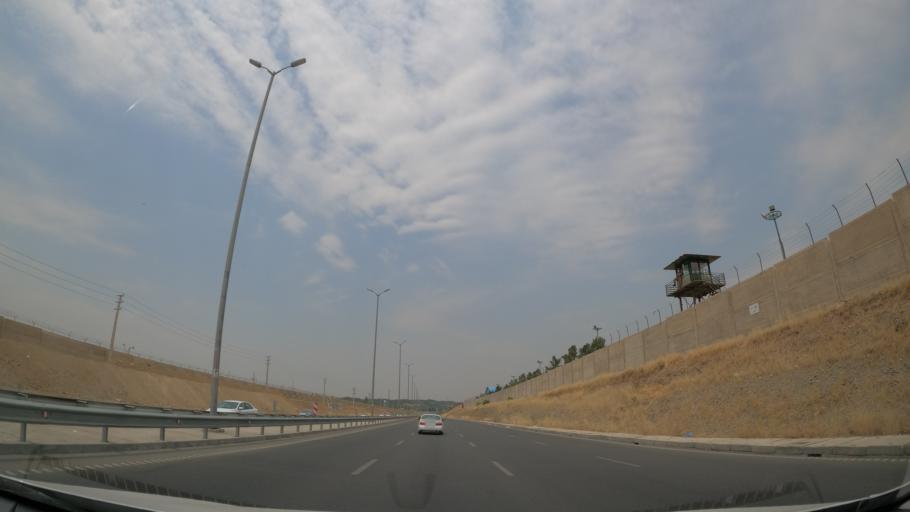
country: IR
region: Tehran
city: Shahr-e Qods
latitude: 35.7404
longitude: 51.2339
